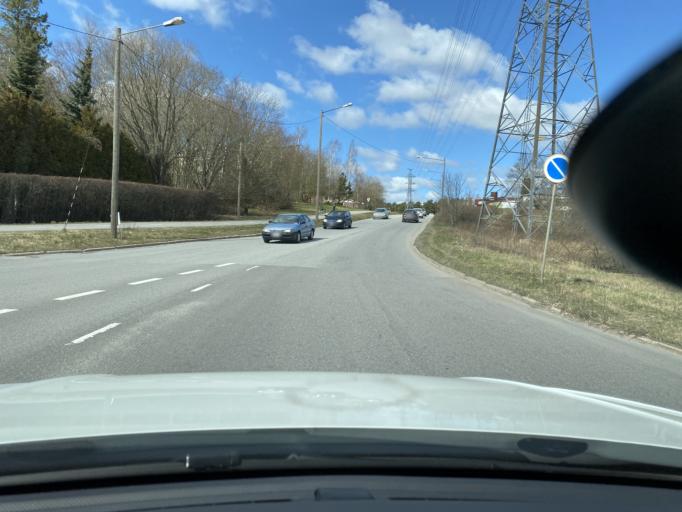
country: FI
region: Varsinais-Suomi
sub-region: Turku
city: Turku
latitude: 60.4725
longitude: 22.2824
